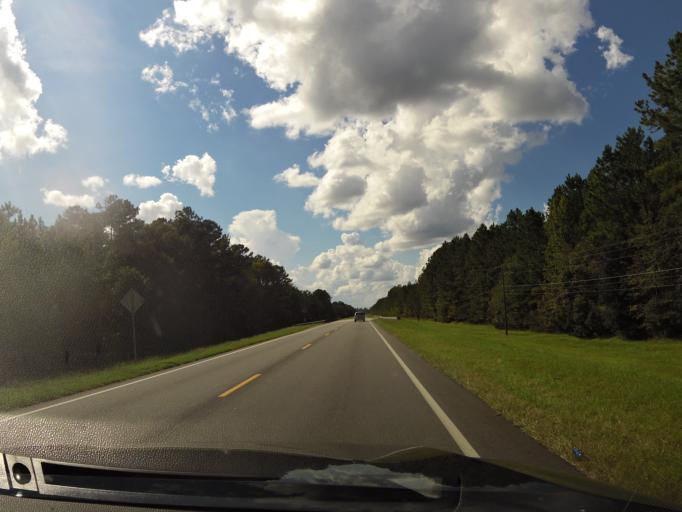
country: US
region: Georgia
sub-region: Echols County
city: Statenville
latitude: 30.7043
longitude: -83.0351
